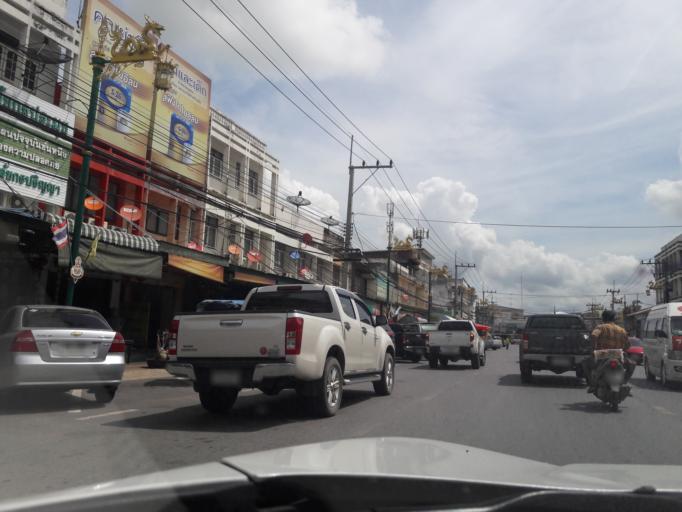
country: TH
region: Lop Buri
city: Khok Samrong
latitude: 15.0660
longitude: 100.7206
